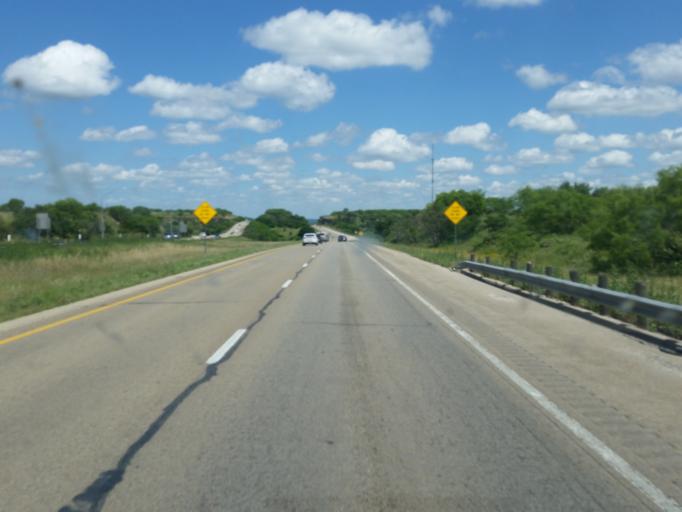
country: US
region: Texas
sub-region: Callahan County
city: Baird
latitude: 32.3978
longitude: -99.3725
